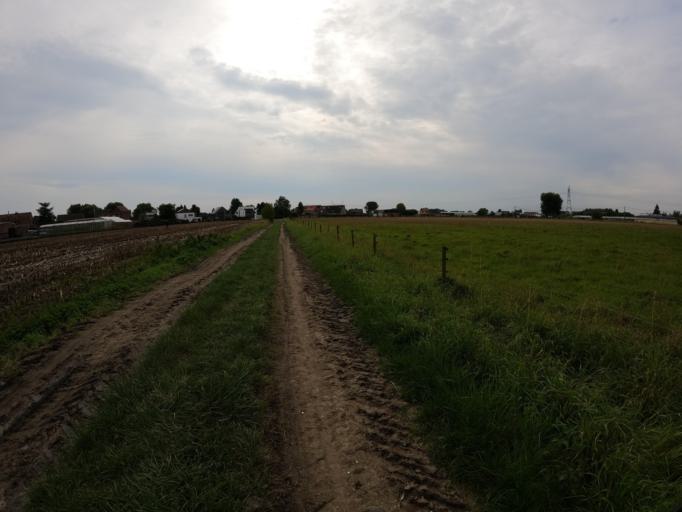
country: BE
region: Flanders
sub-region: Provincie Antwerpen
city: Wommelgem
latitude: 51.1863
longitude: 4.5096
